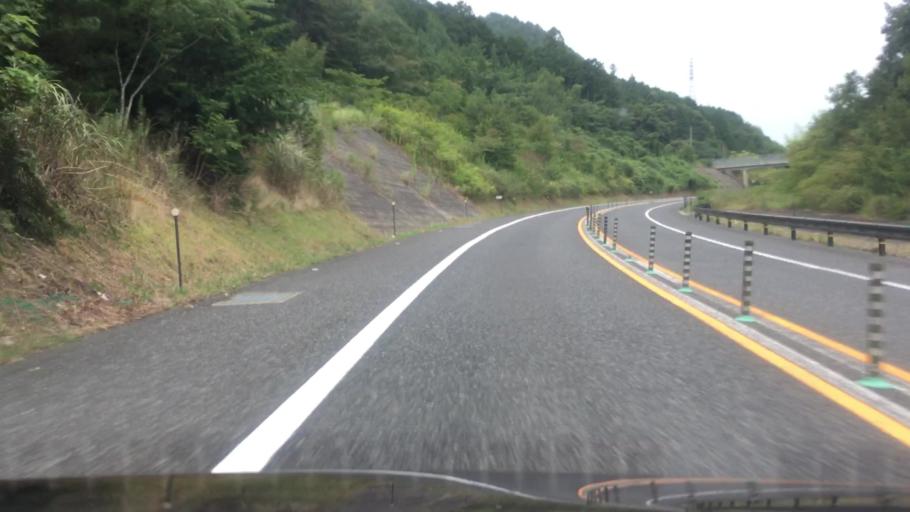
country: JP
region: Kyoto
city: Fukuchiyama
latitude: 35.1617
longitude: 135.0950
